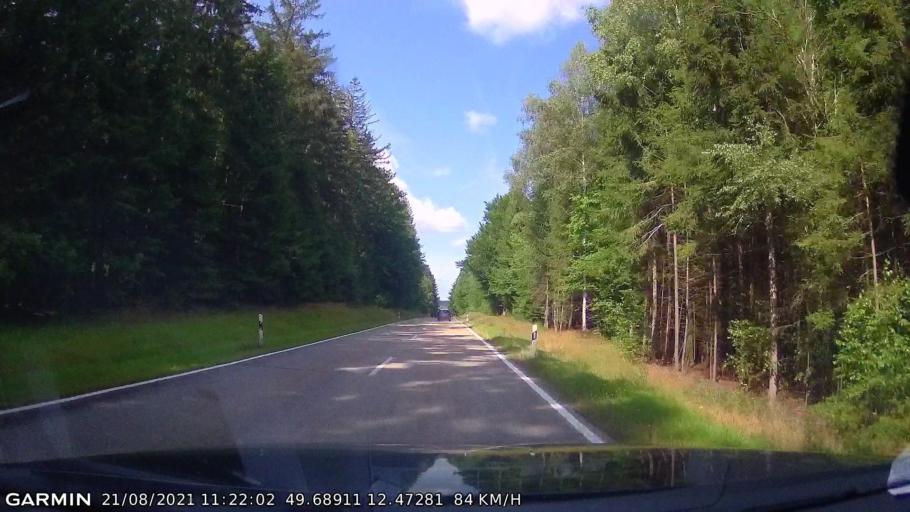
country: DE
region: Bavaria
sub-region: Upper Palatinate
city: Waidhaus
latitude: 49.6891
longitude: 12.4728
